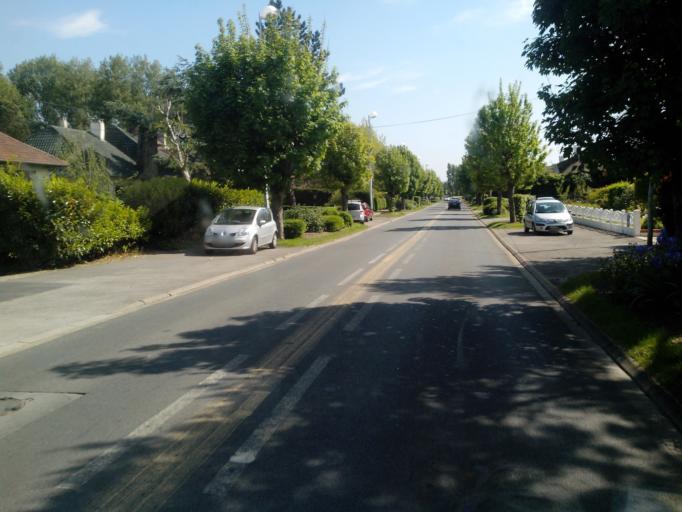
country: FR
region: Nord-Pas-de-Calais
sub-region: Departement du Pas-de-Calais
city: Berck
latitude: 50.4071
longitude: 1.5955
